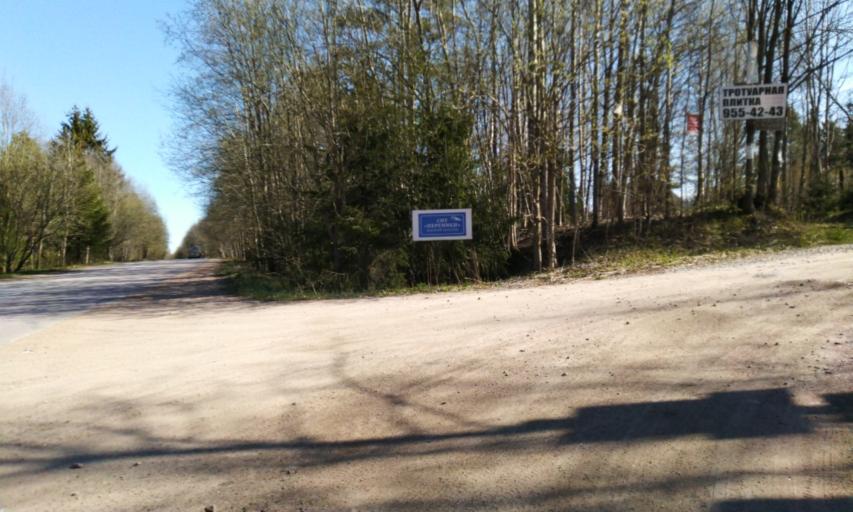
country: RU
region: Leningrad
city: Garbolovo
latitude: 60.3866
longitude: 30.4746
